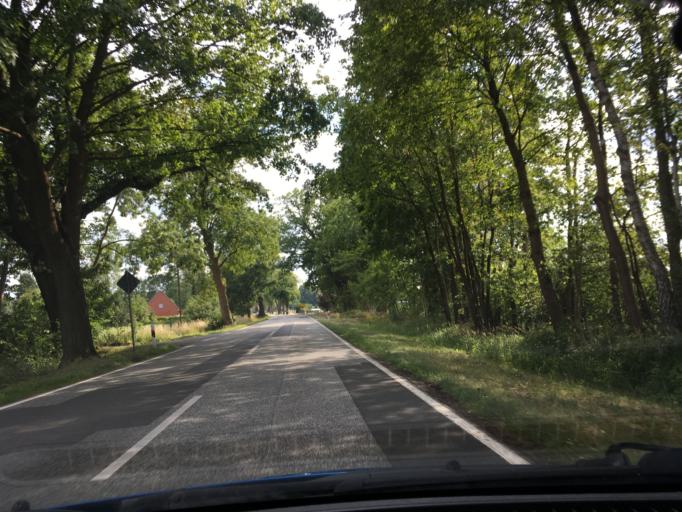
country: DE
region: Mecklenburg-Vorpommern
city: Lubtheen
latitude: 53.3381
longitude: 11.0789
